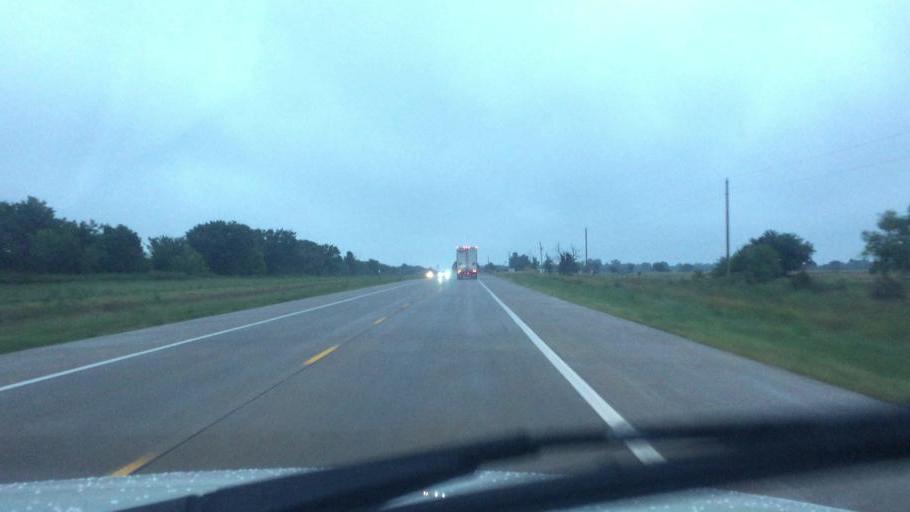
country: US
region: Kansas
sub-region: Neosho County
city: Chanute
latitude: 37.5064
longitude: -95.4709
